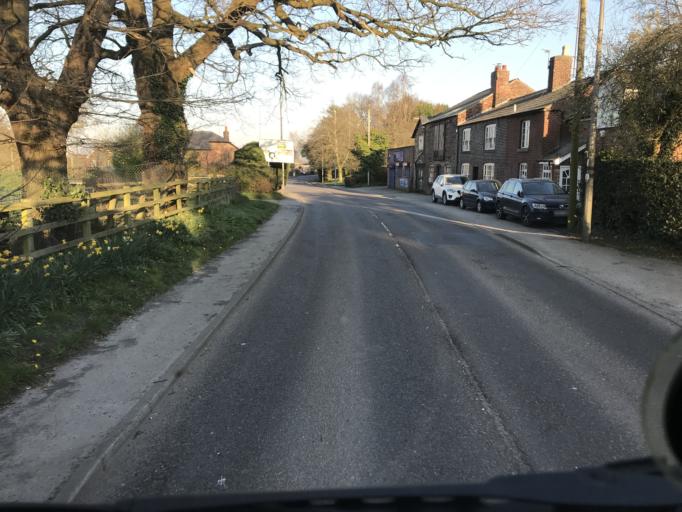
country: GB
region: England
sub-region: Cheshire East
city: Mottram St. Andrew
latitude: 53.3306
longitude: -2.1914
